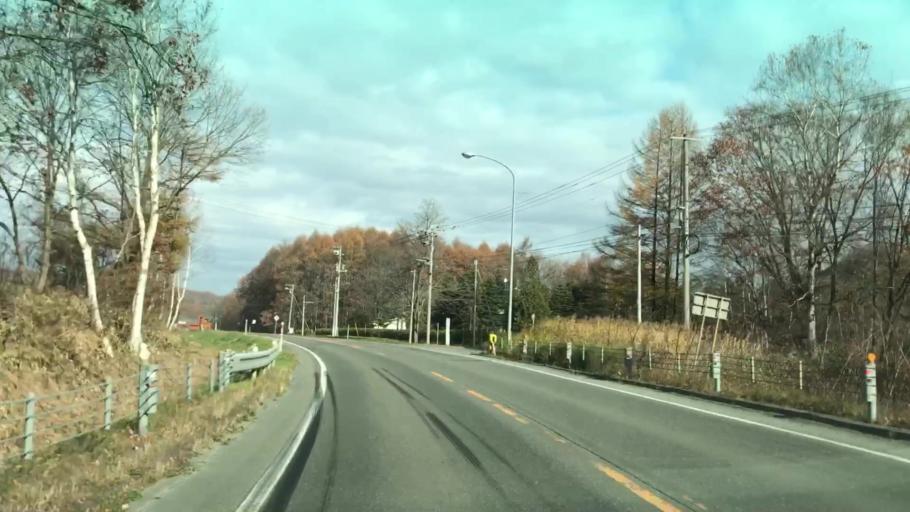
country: JP
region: Hokkaido
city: Shizunai-furukawacho
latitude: 42.6595
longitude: 142.1779
